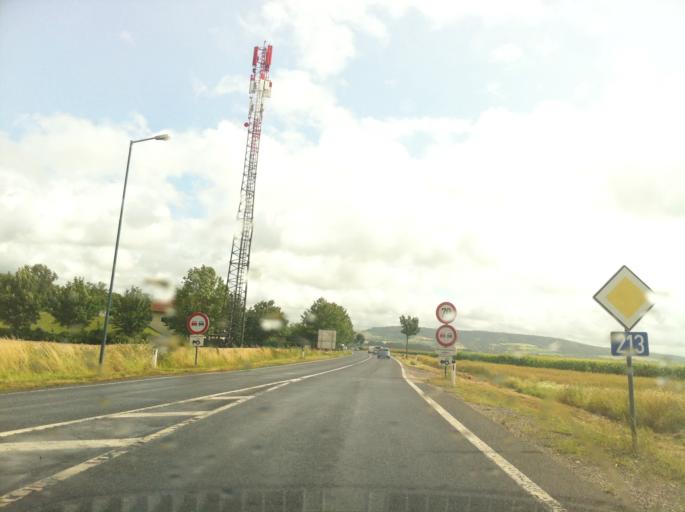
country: AT
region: Lower Austria
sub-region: Politischer Bezirk Tulln
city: Tulln
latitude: 48.3152
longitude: 16.0566
